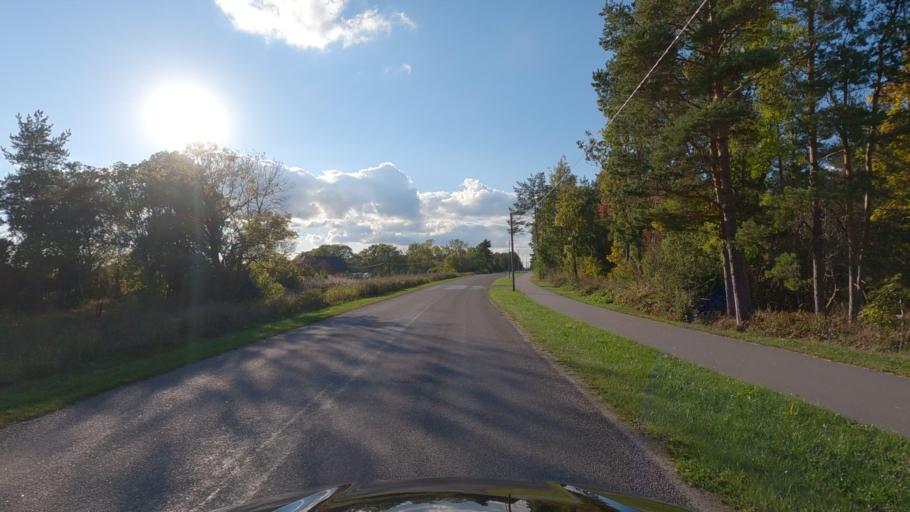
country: EE
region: Harju
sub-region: Saku vald
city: Saku
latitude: 59.3348
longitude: 24.6460
